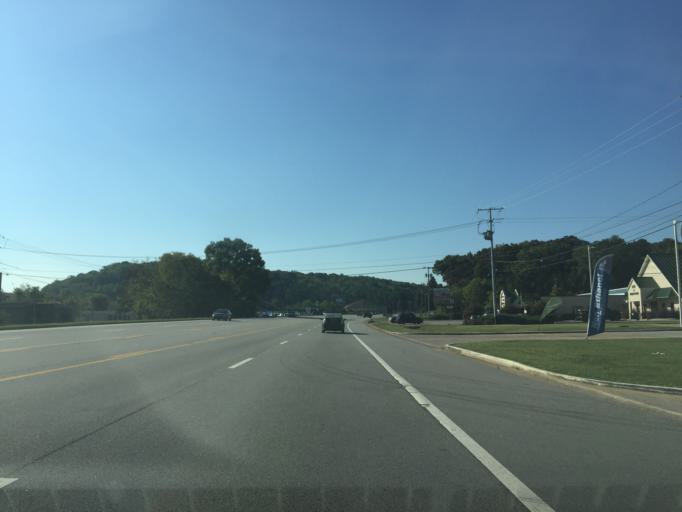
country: US
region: Tennessee
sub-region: Hamilton County
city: Harrison
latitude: 35.1236
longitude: -85.1253
